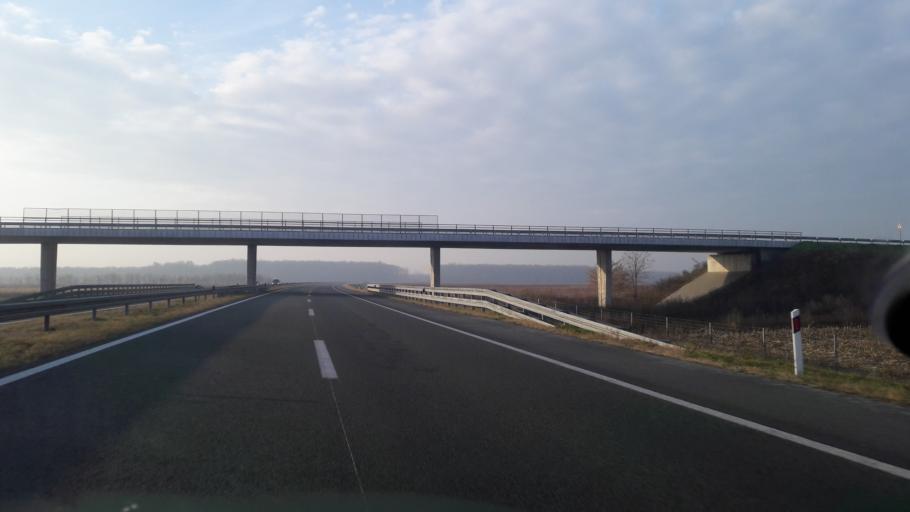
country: HR
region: Osjecko-Baranjska
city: Vuka
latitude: 45.4281
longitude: 18.4567
